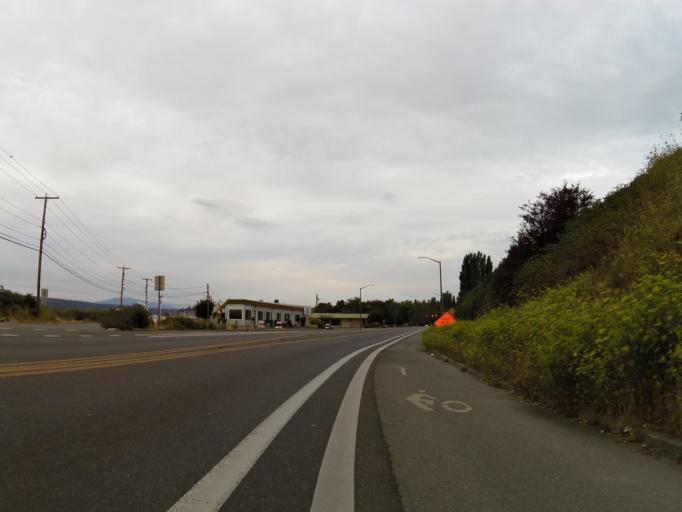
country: US
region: Washington
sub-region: Jefferson County
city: Port Townsend
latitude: 48.1102
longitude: -122.7668
